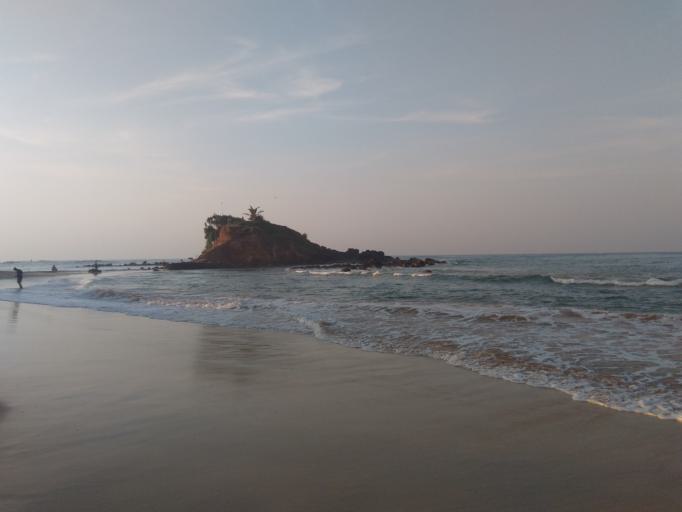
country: LK
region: Southern
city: Weligama
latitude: 5.9430
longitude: 80.4620
